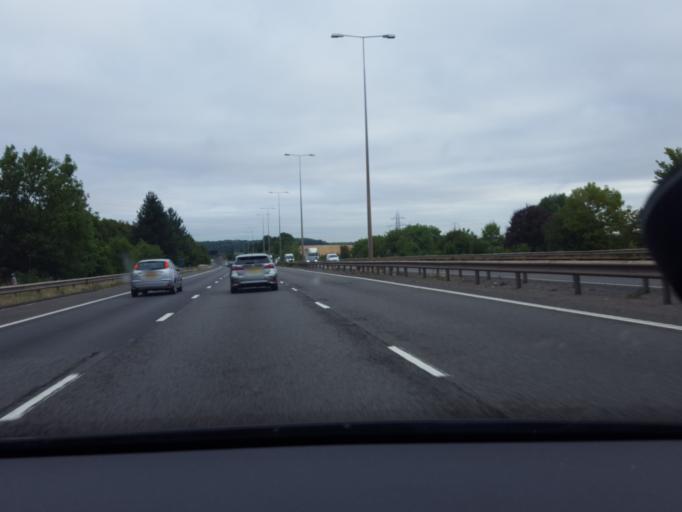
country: GB
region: England
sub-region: Leicestershire
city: Shepshed
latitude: 52.7685
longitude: -1.2756
